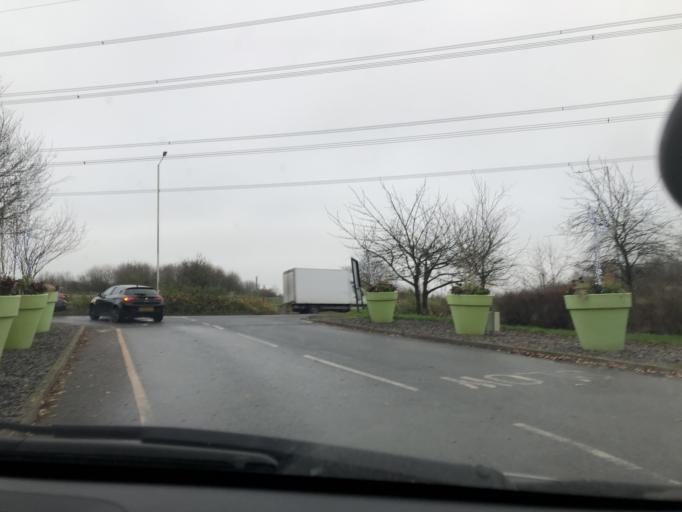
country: GB
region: England
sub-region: Kent
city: Swanscombe
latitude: 51.4257
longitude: 0.3262
